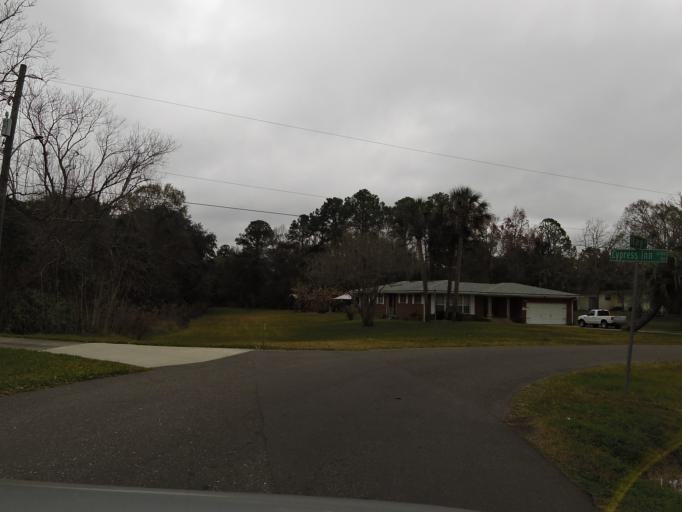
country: US
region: Florida
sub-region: Duval County
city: Jacksonville
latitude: 30.3766
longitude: -81.7202
